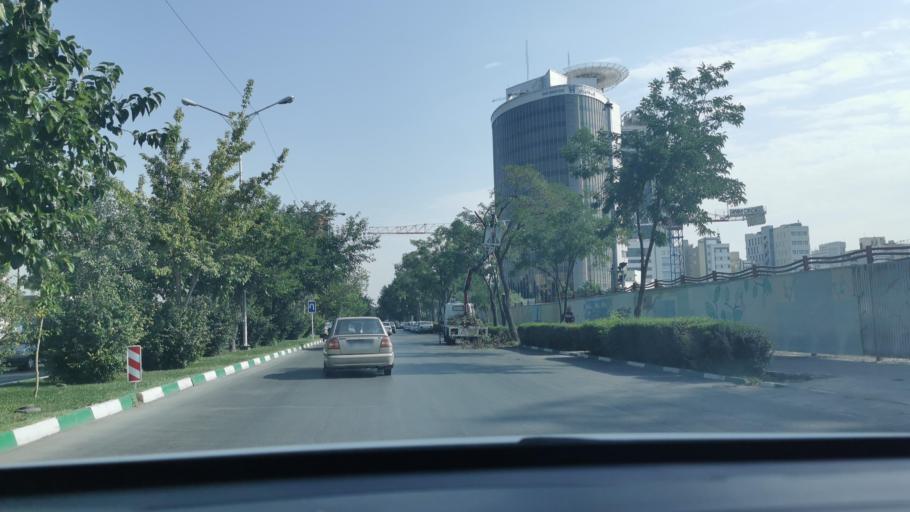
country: IR
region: Razavi Khorasan
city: Mashhad
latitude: 36.3212
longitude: 59.5632
